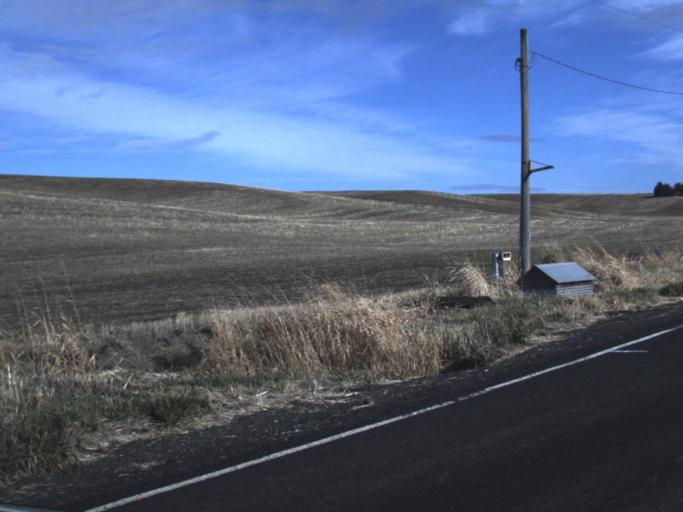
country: US
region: Washington
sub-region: Whitman County
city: Colfax
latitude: 46.9351
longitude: -117.2089
